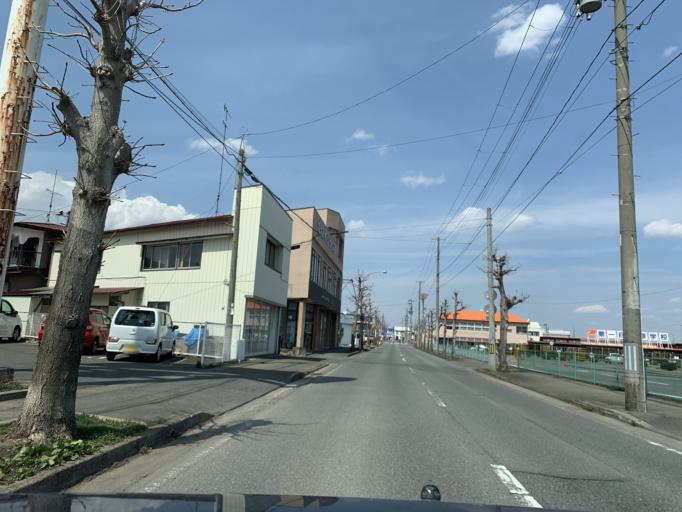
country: JP
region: Iwate
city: Mizusawa
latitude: 39.1487
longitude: 141.1450
